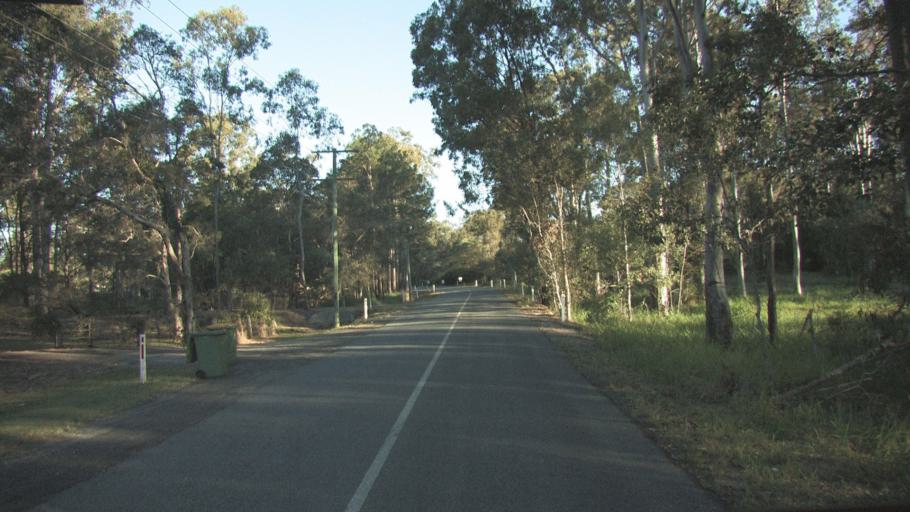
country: AU
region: Queensland
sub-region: Logan
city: Waterford West
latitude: -27.7353
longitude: 153.1454
